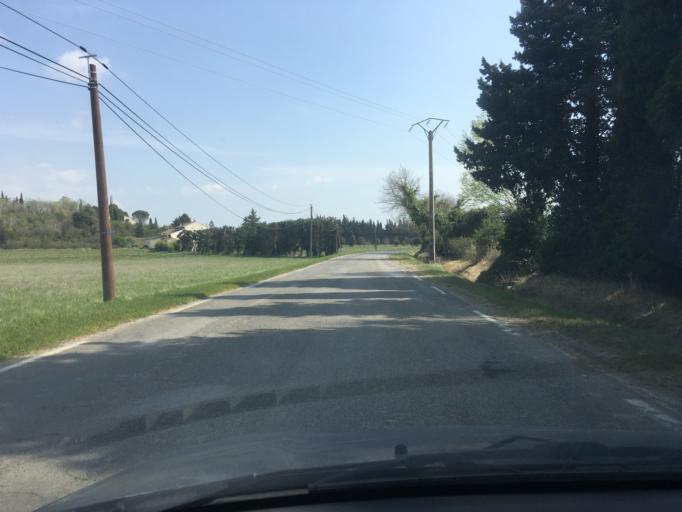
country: FR
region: Provence-Alpes-Cote d'Azur
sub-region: Departement du Vaucluse
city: Aubignan
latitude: 44.1002
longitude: 5.0128
